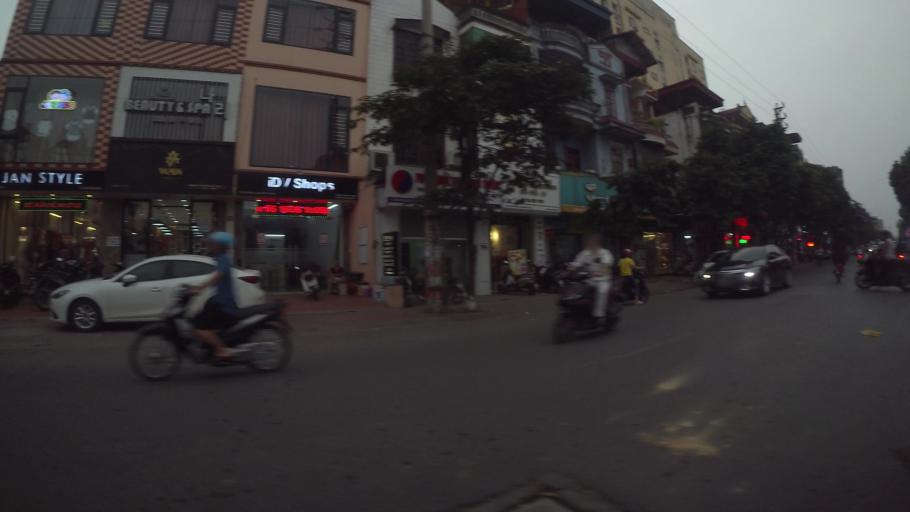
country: VN
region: Ha Noi
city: Trau Quy
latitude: 21.0356
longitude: 105.9108
